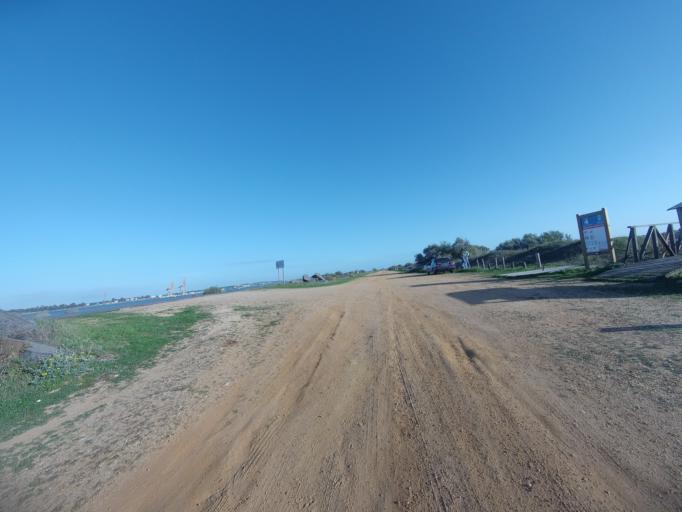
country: ES
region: Andalusia
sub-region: Provincia de Huelva
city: Punta Umbria
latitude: 37.1500
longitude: -6.8963
